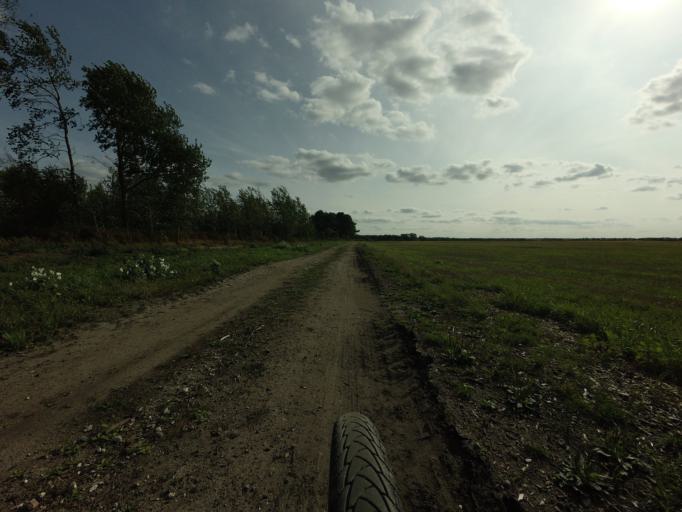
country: DK
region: Zealand
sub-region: Vordingborg Kommune
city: Praesto
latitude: 55.1484
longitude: 12.0923
